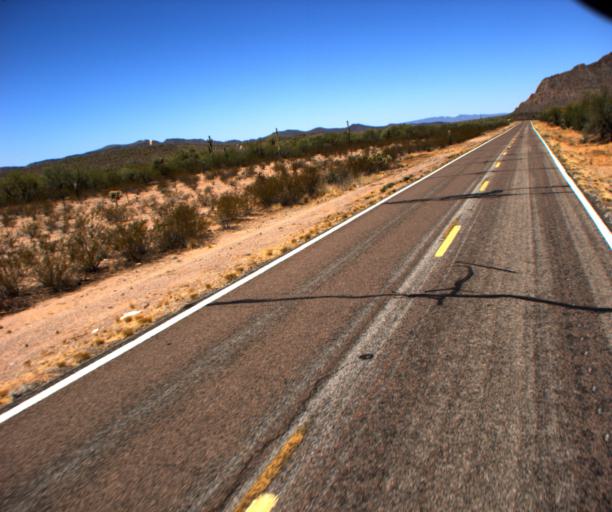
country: US
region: Arizona
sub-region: Pima County
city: Ajo
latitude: 32.2223
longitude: -112.6707
